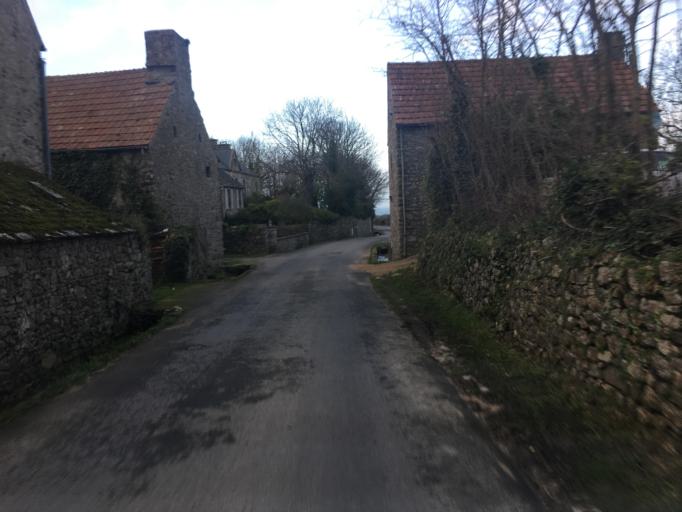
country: FR
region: Lower Normandy
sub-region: Departement de la Manche
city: Beaumont-Hague
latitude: 49.7139
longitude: -1.9220
